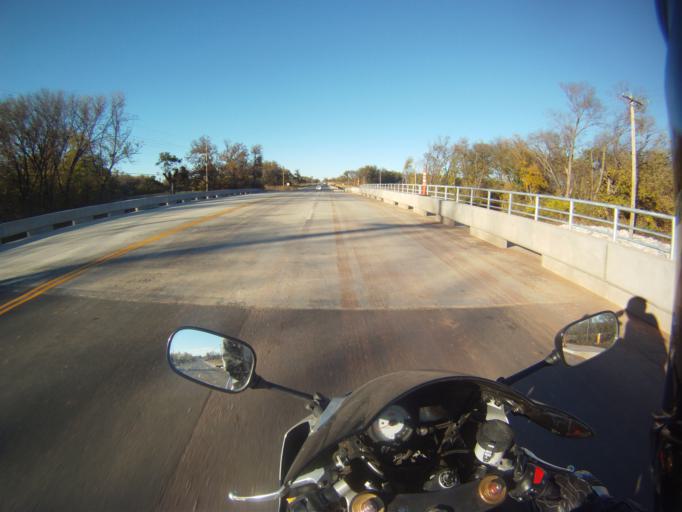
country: US
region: Oklahoma
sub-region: Payne County
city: Stillwater
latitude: 36.1232
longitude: -97.1231
